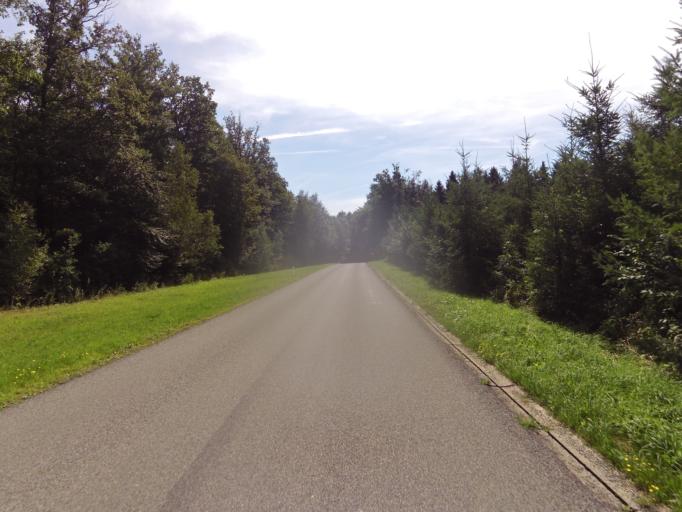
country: BE
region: Wallonia
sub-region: Province du Luxembourg
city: Saint-Hubert
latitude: 50.0429
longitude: 5.3548
